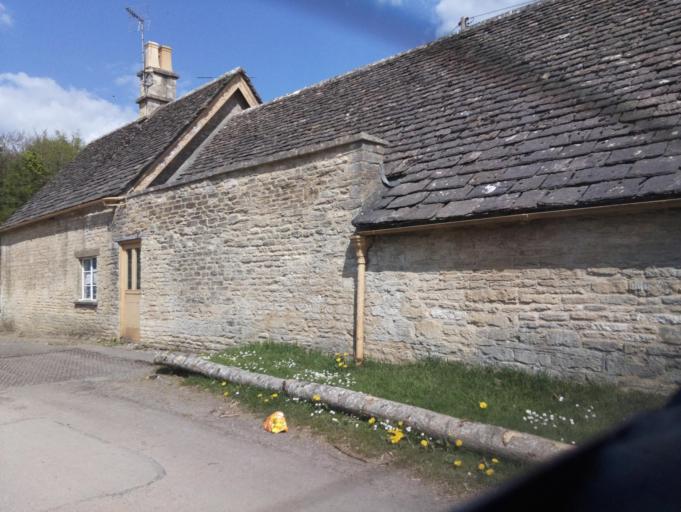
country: GB
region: England
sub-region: Wiltshire
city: Luckington
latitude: 51.5445
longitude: -2.2843
